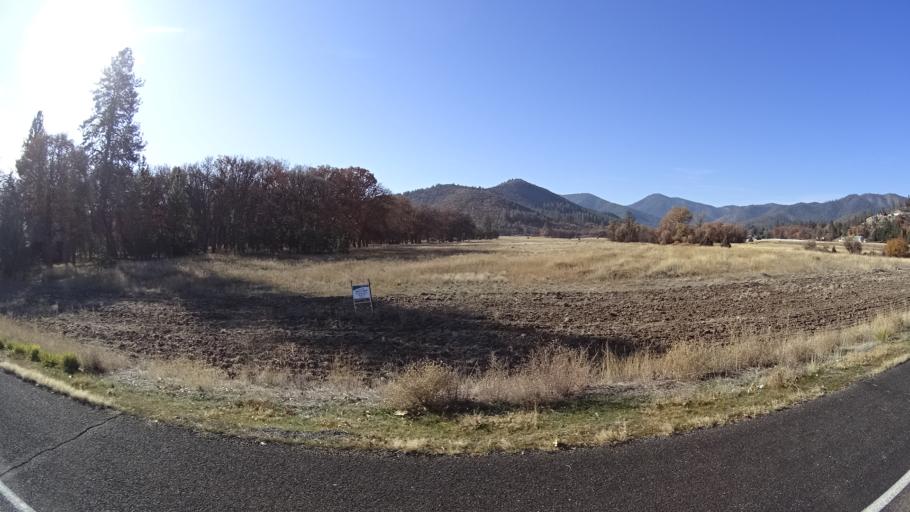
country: US
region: California
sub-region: Siskiyou County
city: Yreka
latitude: 41.6951
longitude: -122.6424
